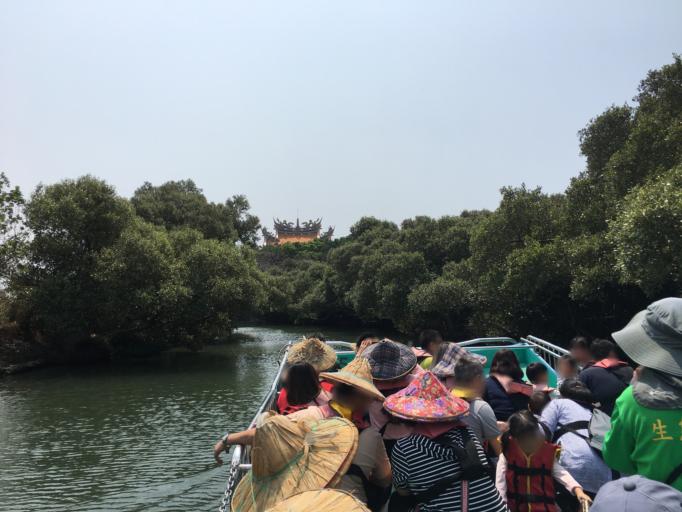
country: TW
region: Taiwan
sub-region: Tainan
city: Tainan
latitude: 23.0214
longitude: 120.1346
